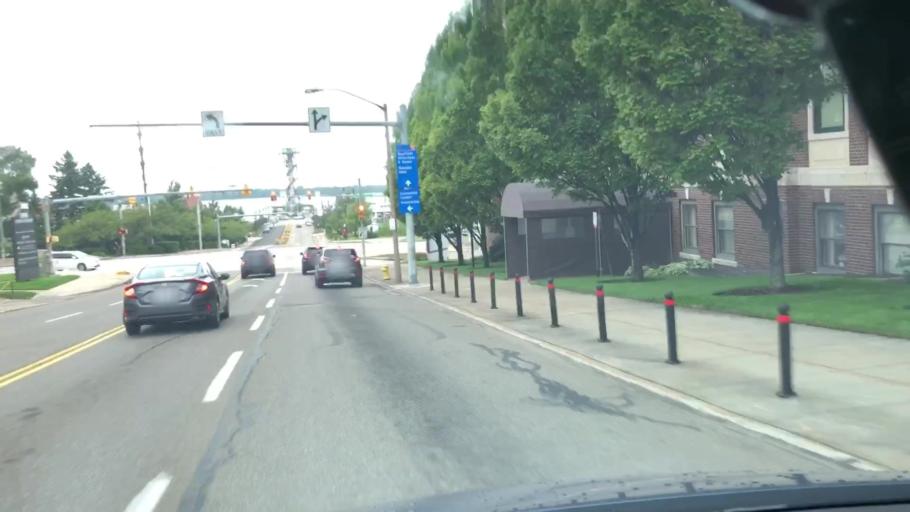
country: US
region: Pennsylvania
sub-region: Erie County
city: Erie
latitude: 42.1336
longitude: -80.0880
